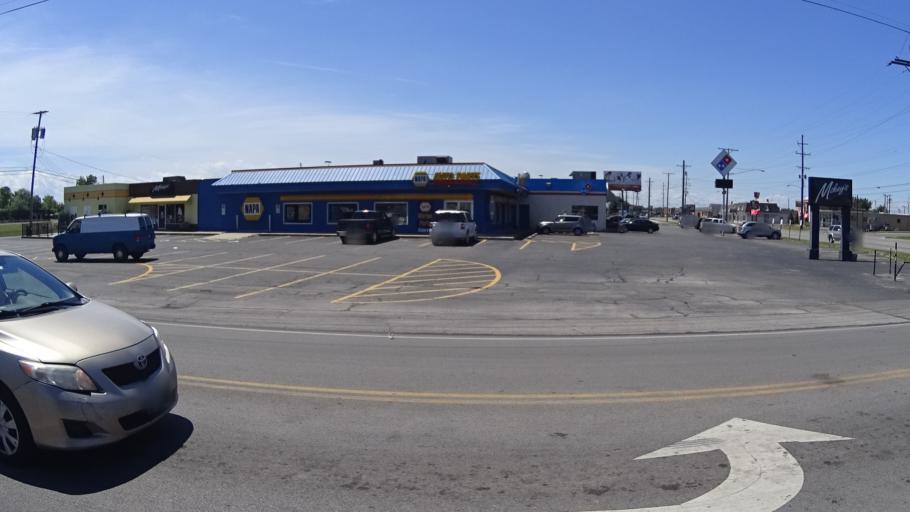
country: US
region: Ohio
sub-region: Erie County
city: Sandusky
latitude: 41.4327
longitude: -82.7053
